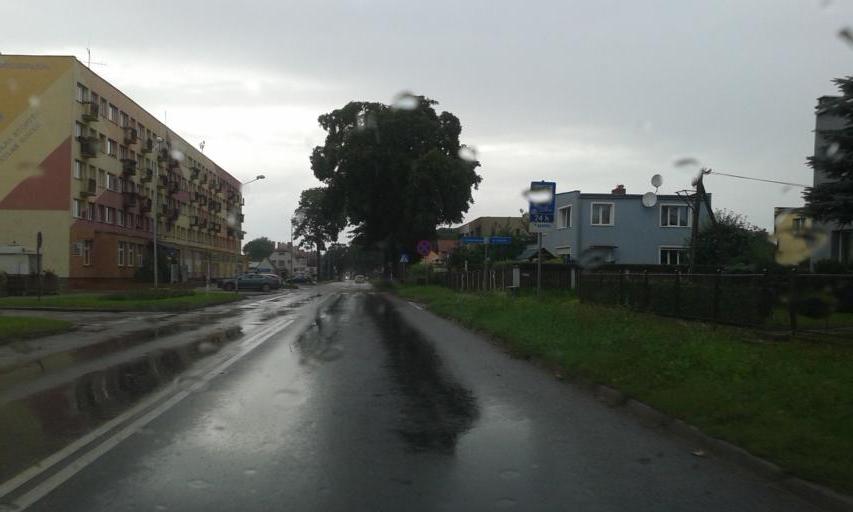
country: PL
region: West Pomeranian Voivodeship
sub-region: Powiat drawski
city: Czaplinek
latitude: 53.5511
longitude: 16.2408
